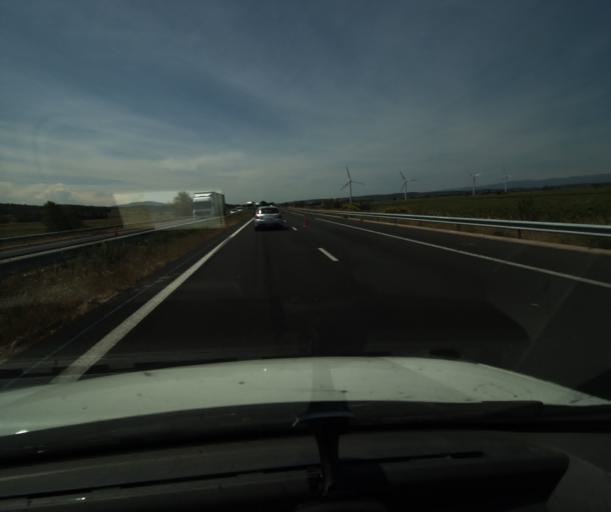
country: FR
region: Languedoc-Roussillon
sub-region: Departement de l'Aude
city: Ornaisons
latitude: 43.1676
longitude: 2.8216
